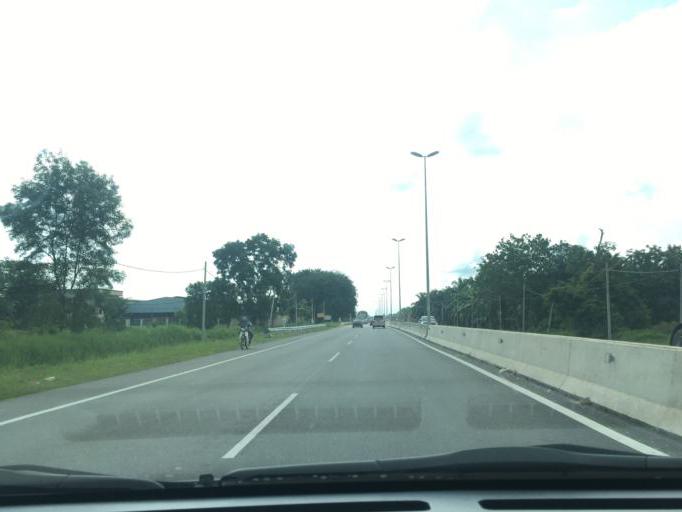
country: MY
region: Selangor
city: Batu Arang
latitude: 3.3073
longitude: 101.4261
